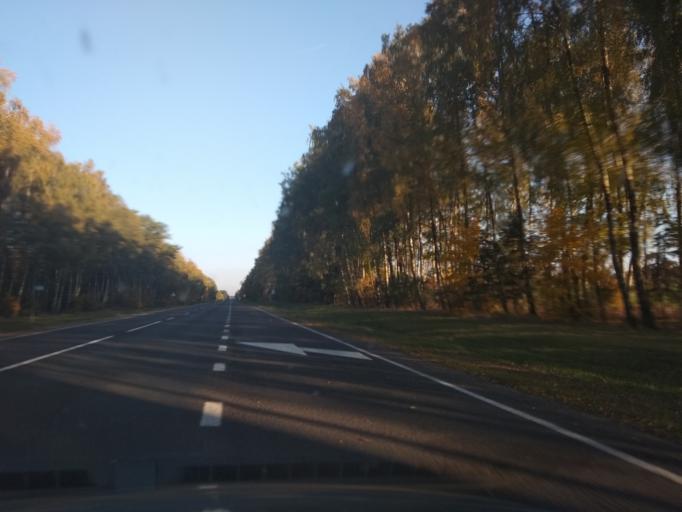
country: BY
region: Grodnenskaya
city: Vawkavysk
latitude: 53.1495
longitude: 24.5678
